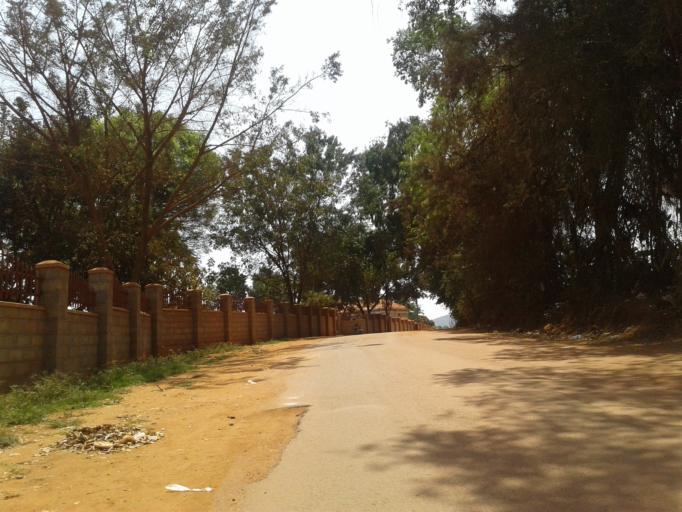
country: UG
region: Central Region
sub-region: Kampala District
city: Kampala
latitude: 0.2649
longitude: 32.6299
